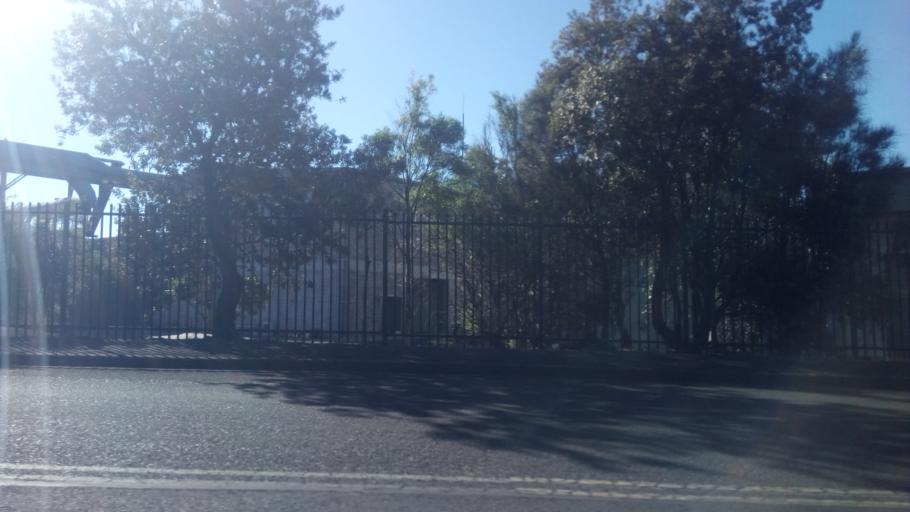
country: AU
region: New South Wales
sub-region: Wollongong
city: Coniston
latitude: -34.4450
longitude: 150.8980
